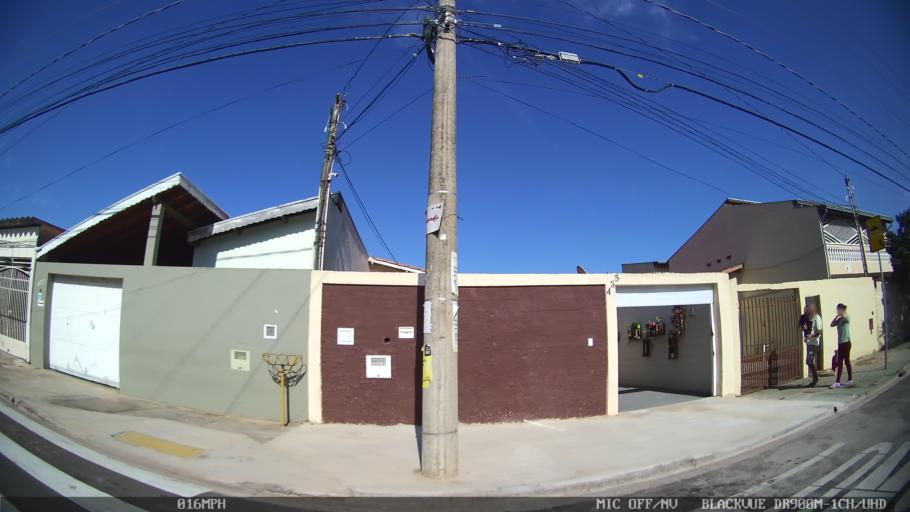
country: BR
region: Sao Paulo
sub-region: Campinas
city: Campinas
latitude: -22.9466
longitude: -47.1202
